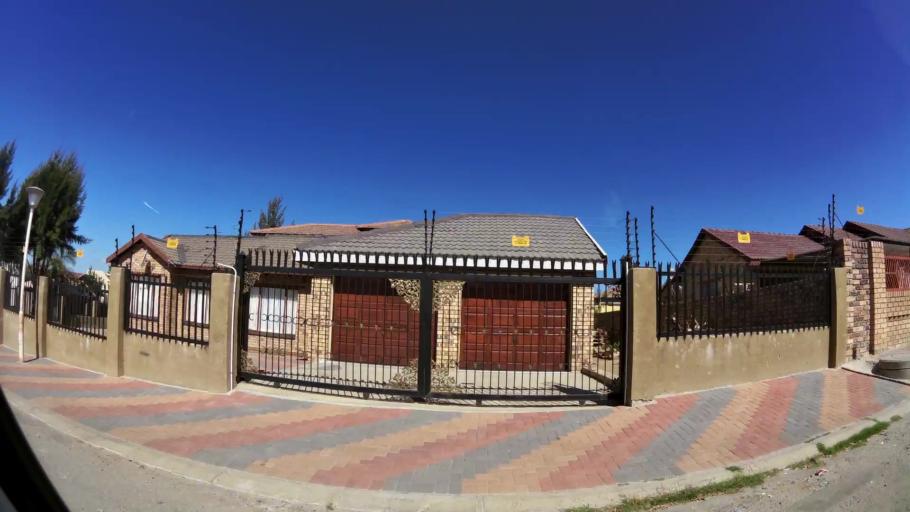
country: ZA
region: Limpopo
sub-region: Capricorn District Municipality
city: Polokwane
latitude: -23.8689
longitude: 29.4314
